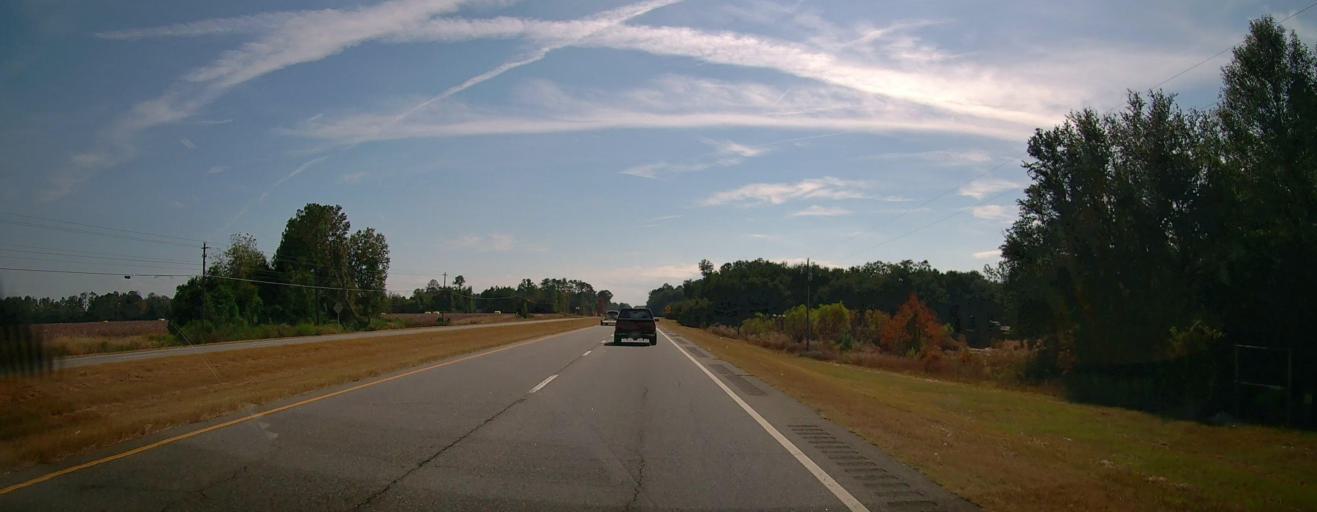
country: US
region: Georgia
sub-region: Dougherty County
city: Putney
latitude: 31.4936
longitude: -84.1160
